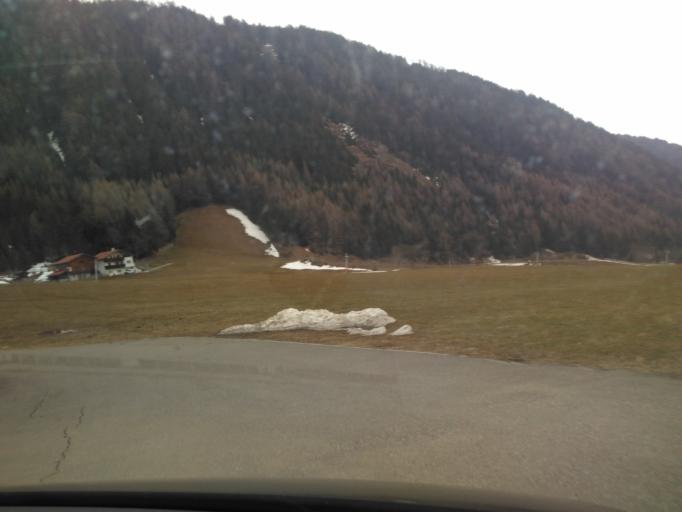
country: IT
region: Trentino-Alto Adige
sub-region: Bolzano
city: Fortezza
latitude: 46.8383
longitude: 11.6275
